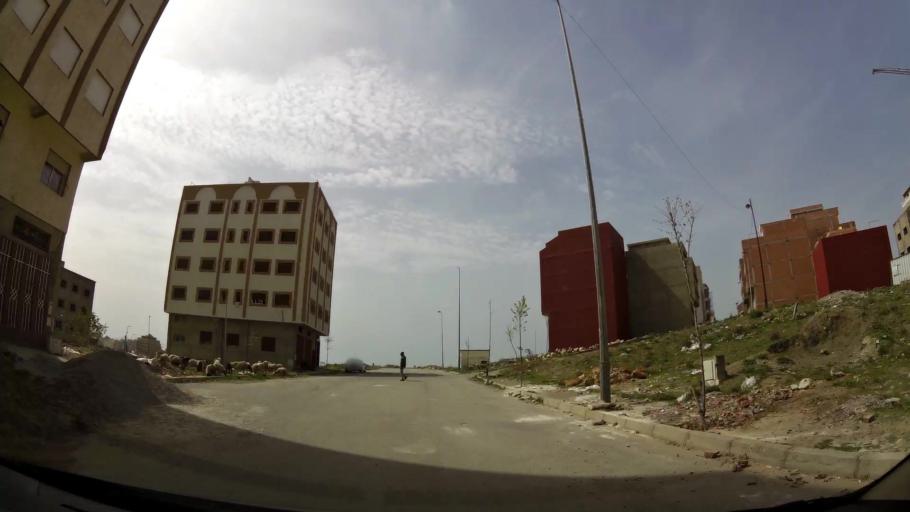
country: MA
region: Tanger-Tetouan
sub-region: Tanger-Assilah
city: Tangier
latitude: 35.7389
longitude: -5.8377
